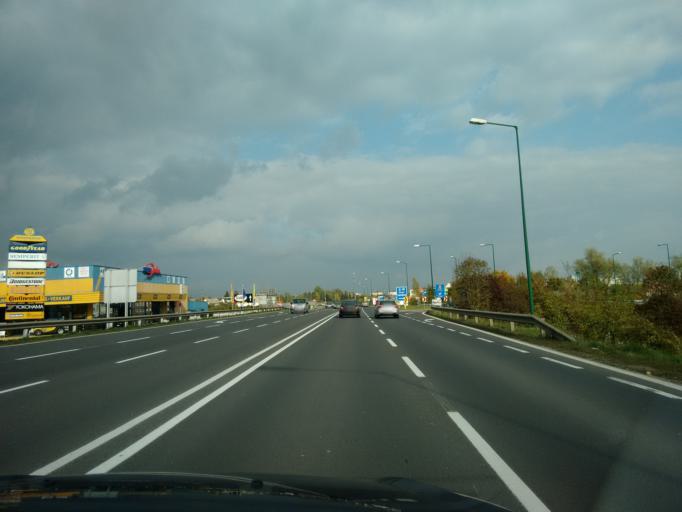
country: AT
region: Upper Austria
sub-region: Wels-Land
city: Gunskirchen
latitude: 48.1499
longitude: 13.9788
